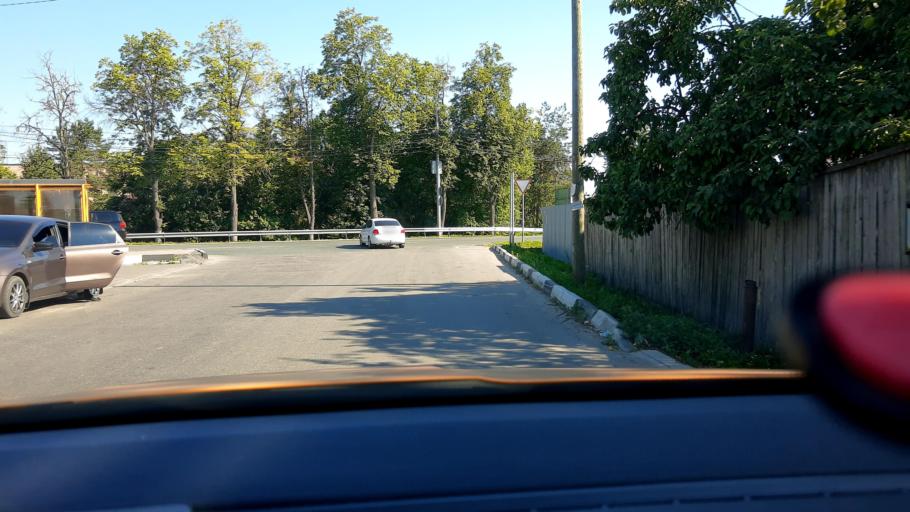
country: RU
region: Moskovskaya
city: Arkhangel'skoye
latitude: 55.7988
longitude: 37.3068
